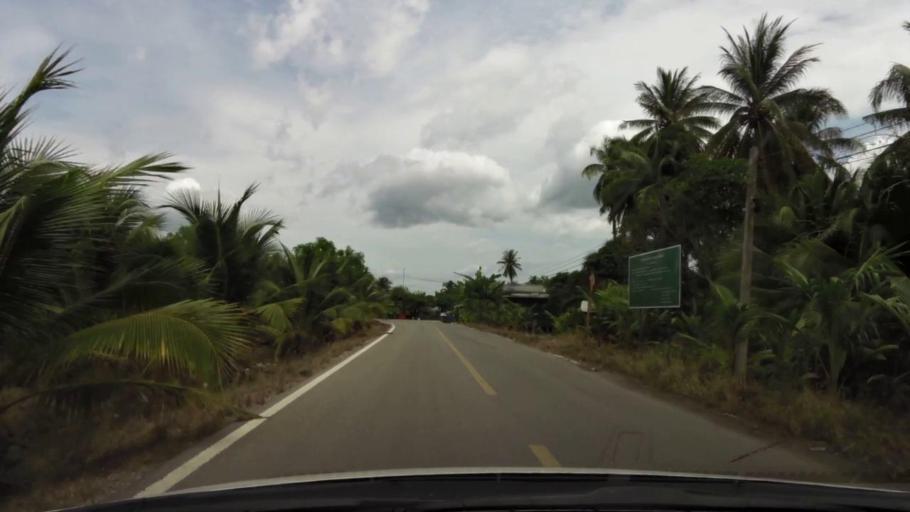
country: TH
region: Ratchaburi
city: Damnoen Saduak
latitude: 13.5223
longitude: 100.0161
